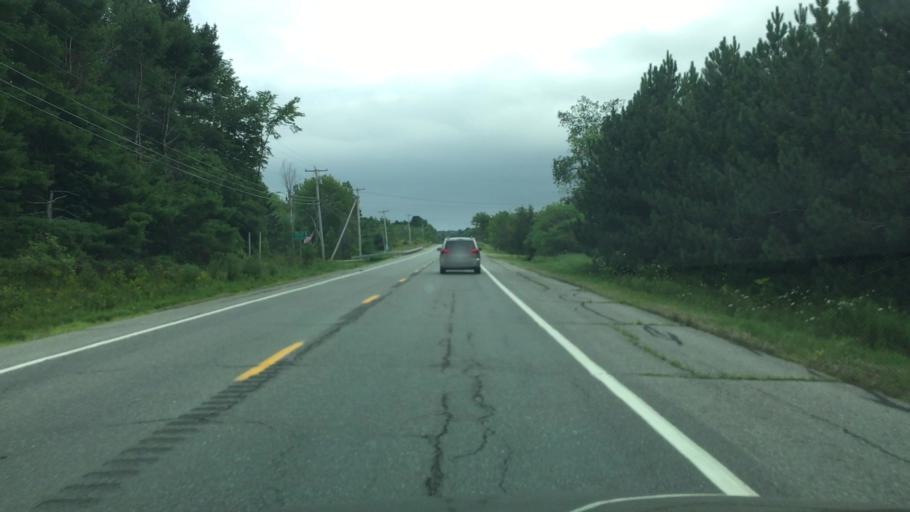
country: US
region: Maine
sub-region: Waldo County
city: Stockton Springs
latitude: 44.5356
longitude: -68.8611
